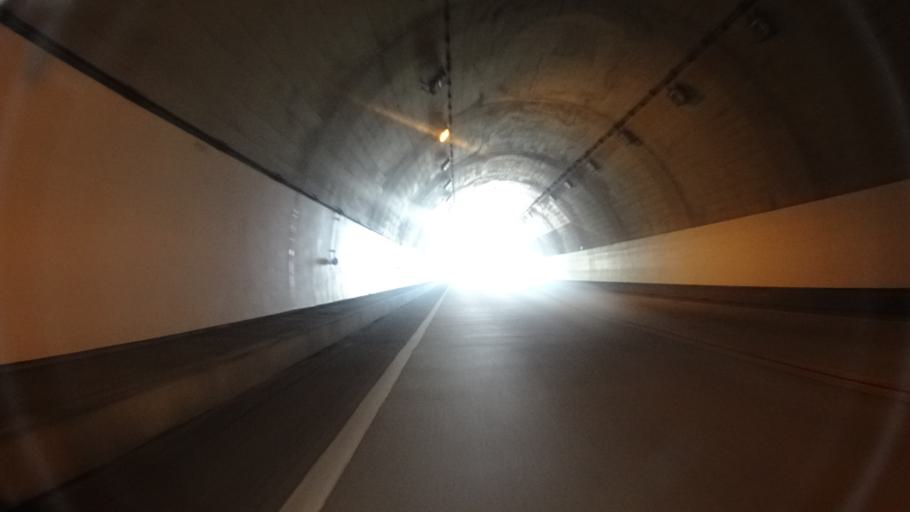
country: JP
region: Yamanashi
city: Enzan
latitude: 35.7531
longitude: 138.8104
